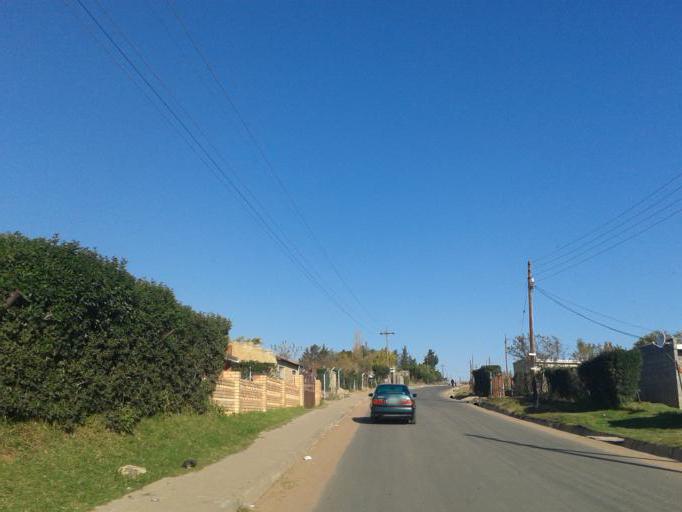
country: LS
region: Maseru
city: Maseru
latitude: -29.2799
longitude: 27.5347
